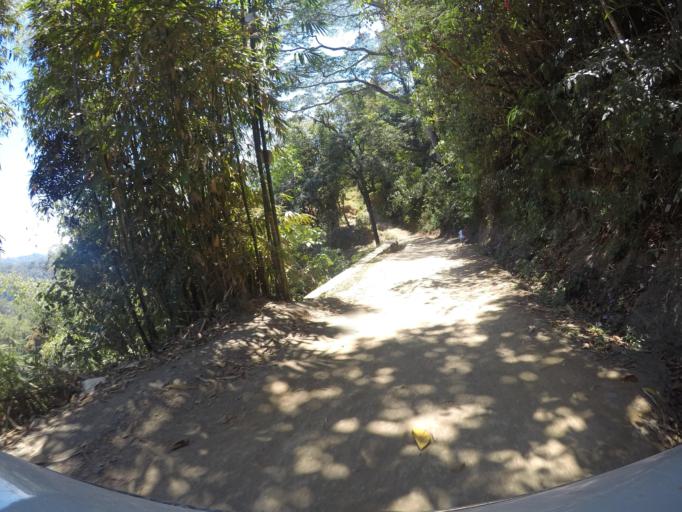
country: TL
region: Ermera
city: Gleno
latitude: -8.7458
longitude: 125.4021
